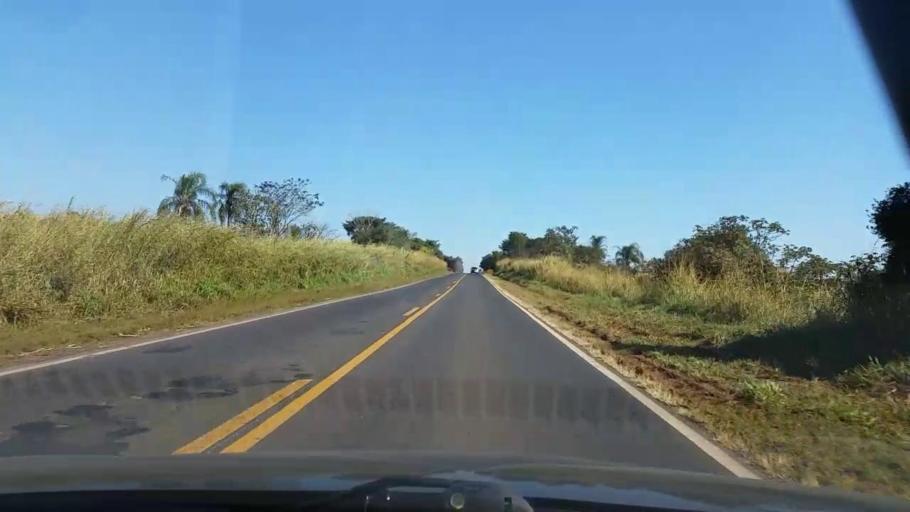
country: BR
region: Sao Paulo
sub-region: Avare
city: Avare
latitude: -22.9130
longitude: -48.7760
